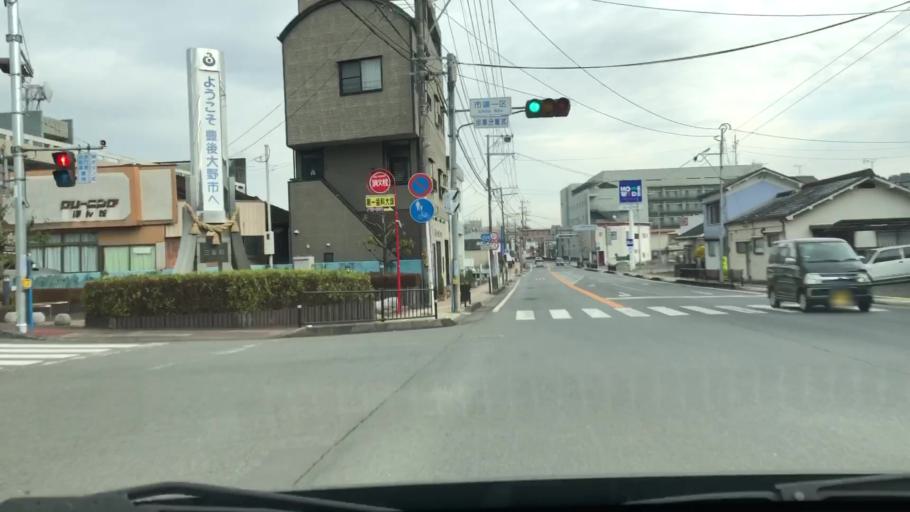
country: JP
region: Oita
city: Takedamachi
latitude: 32.9761
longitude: 131.5820
